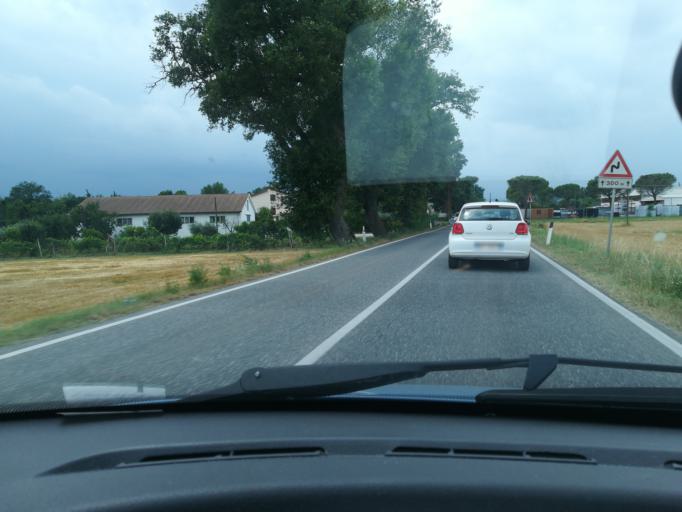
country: IT
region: The Marches
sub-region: Provincia di Macerata
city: Montecassiano
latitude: 43.3412
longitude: 13.4419
